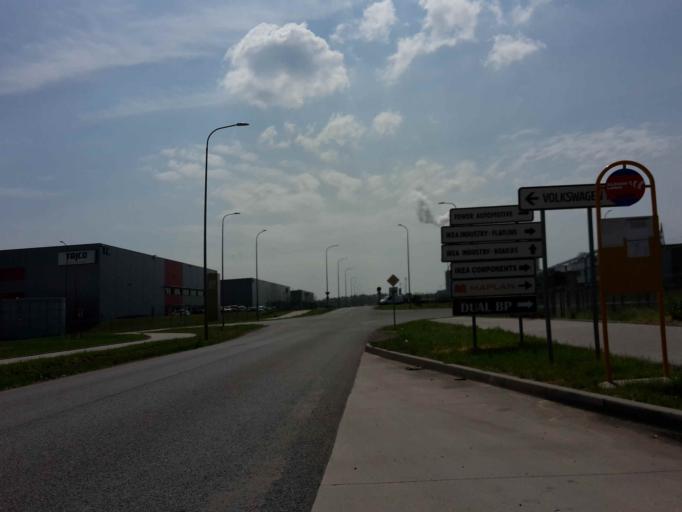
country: SK
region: Bratislavsky
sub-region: Okres Malacky
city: Malacky
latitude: 48.4221
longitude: 17.0358
